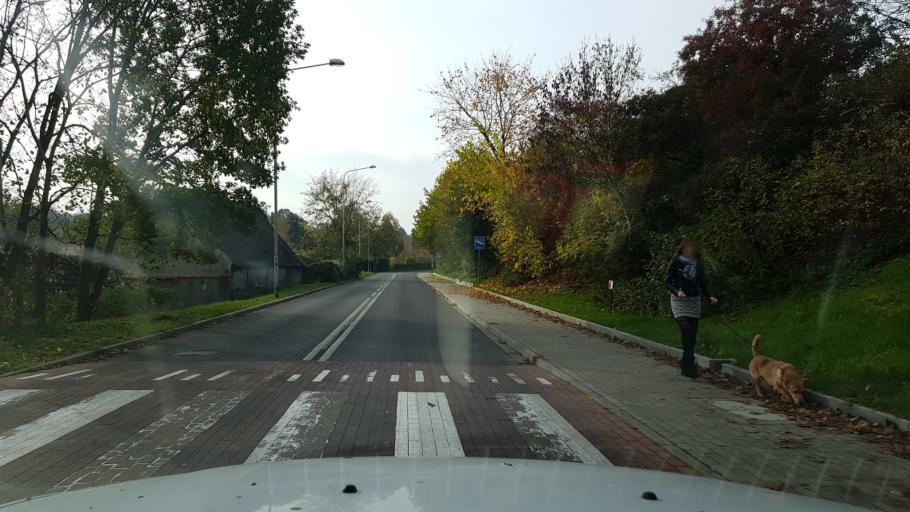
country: PL
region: West Pomeranian Voivodeship
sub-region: Powiat swidwinski
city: Polczyn-Zdroj
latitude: 53.7657
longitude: 16.0898
